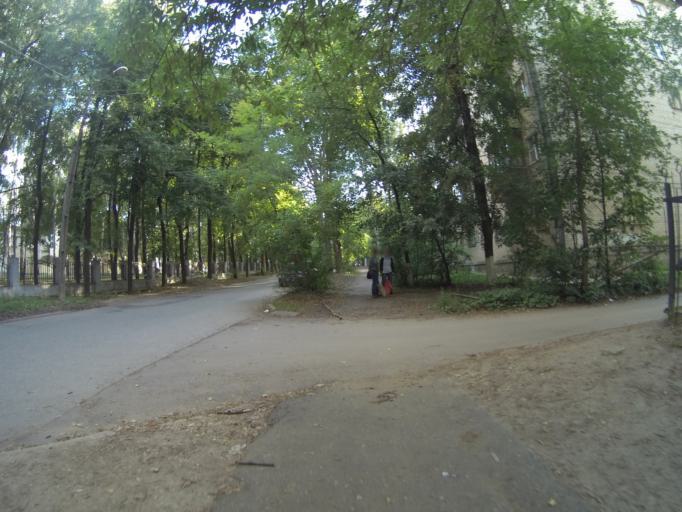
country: RU
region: Vladimir
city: Vladimir
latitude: 56.1472
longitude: 40.4259
